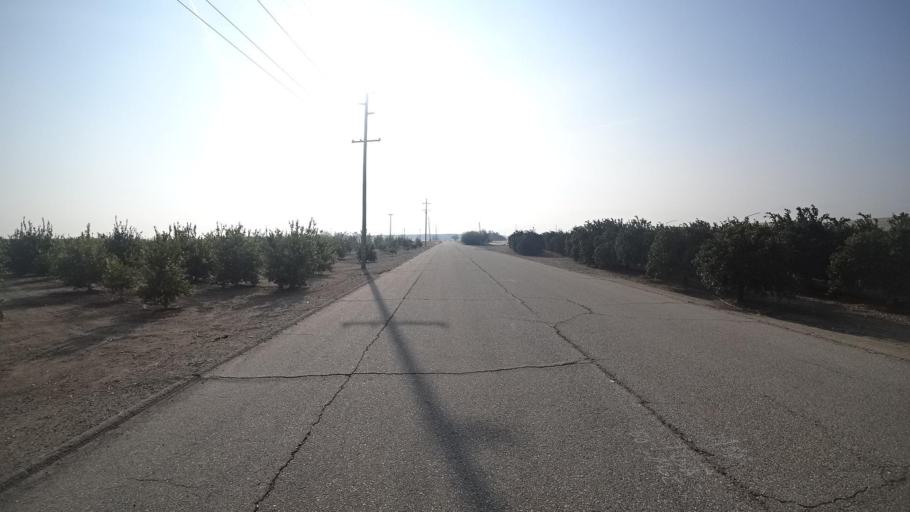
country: US
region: California
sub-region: Kern County
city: Frazier Park
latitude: 35.0086
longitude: -118.9507
